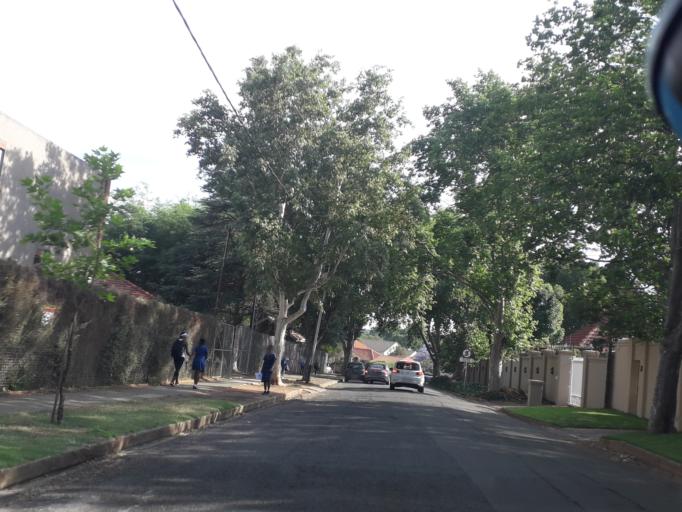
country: ZA
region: Gauteng
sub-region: City of Johannesburg Metropolitan Municipality
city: Johannesburg
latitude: -26.1570
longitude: 28.0229
